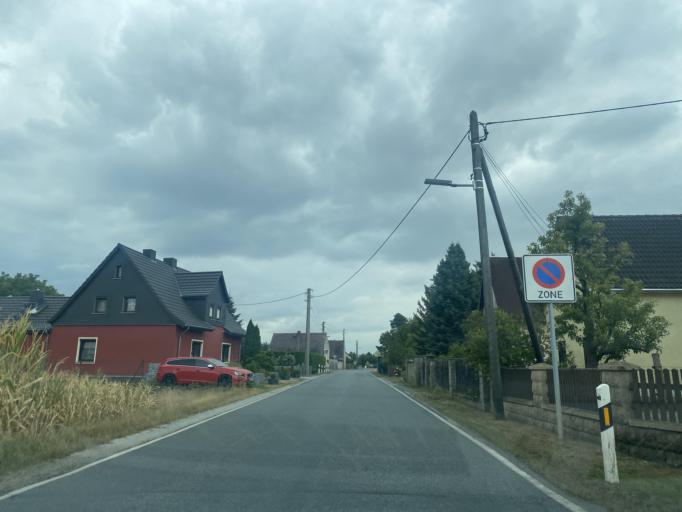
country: DE
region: Saxony
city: Konigswartha
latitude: 51.2996
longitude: 14.3166
